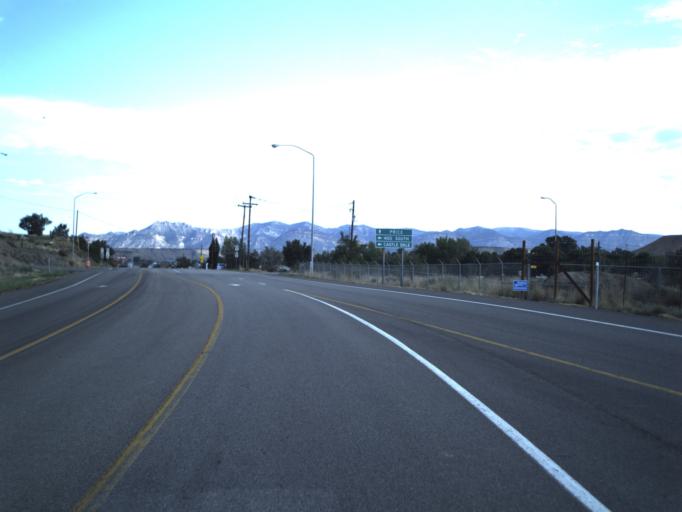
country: US
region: Utah
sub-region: Carbon County
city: Price
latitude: 39.5878
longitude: -110.7889
